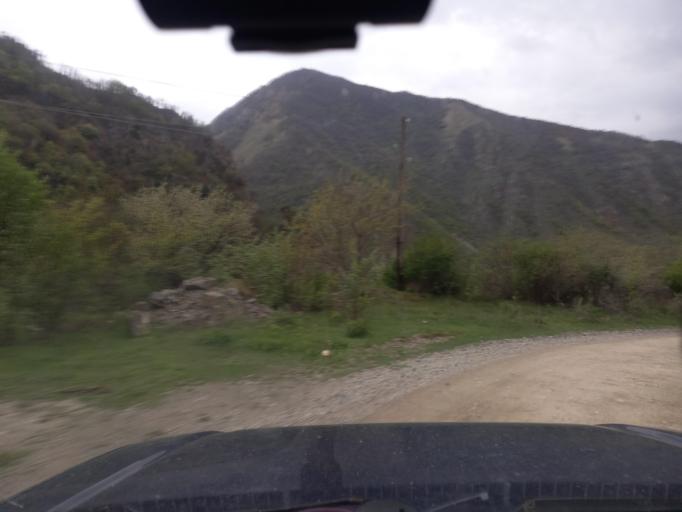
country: RU
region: North Ossetia
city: Mizur
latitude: 42.8468
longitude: 44.1651
